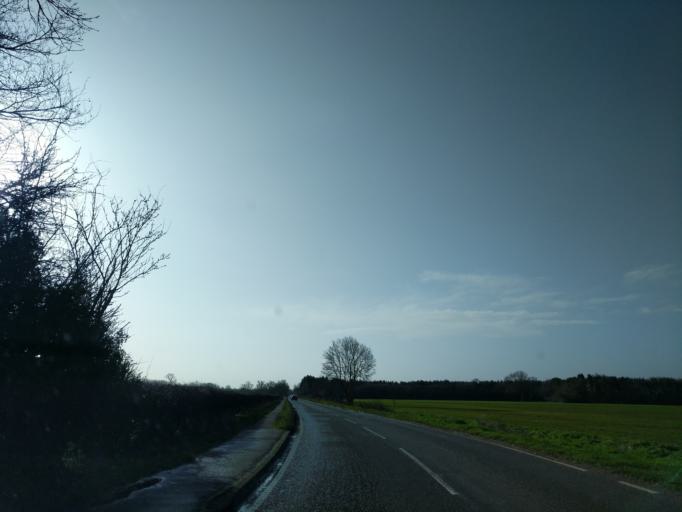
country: GB
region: England
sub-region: Cambridgeshire
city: Hemingford Grey
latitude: 52.3117
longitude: -0.0743
